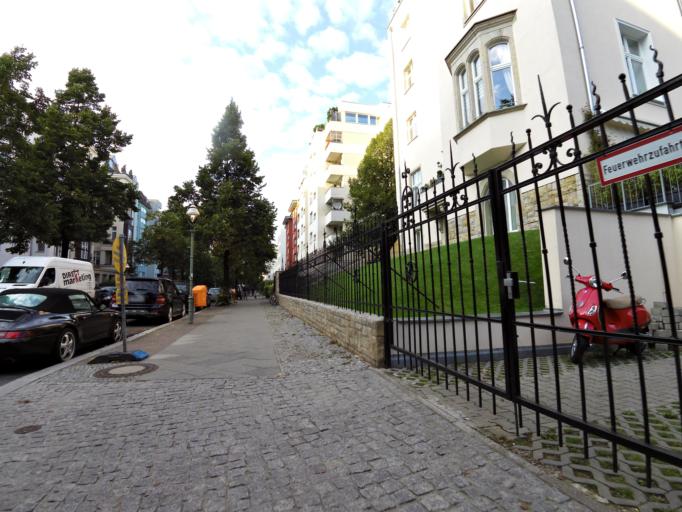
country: DE
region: Berlin
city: Wilmersdorf Bezirk
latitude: 52.4884
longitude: 13.3288
